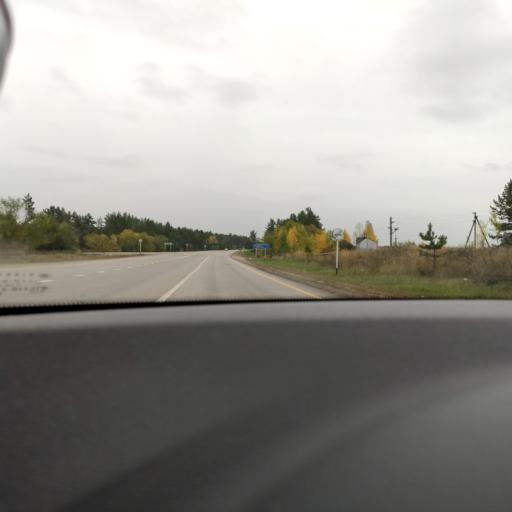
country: RU
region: Samara
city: Mirnyy
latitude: 53.5391
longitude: 50.2993
